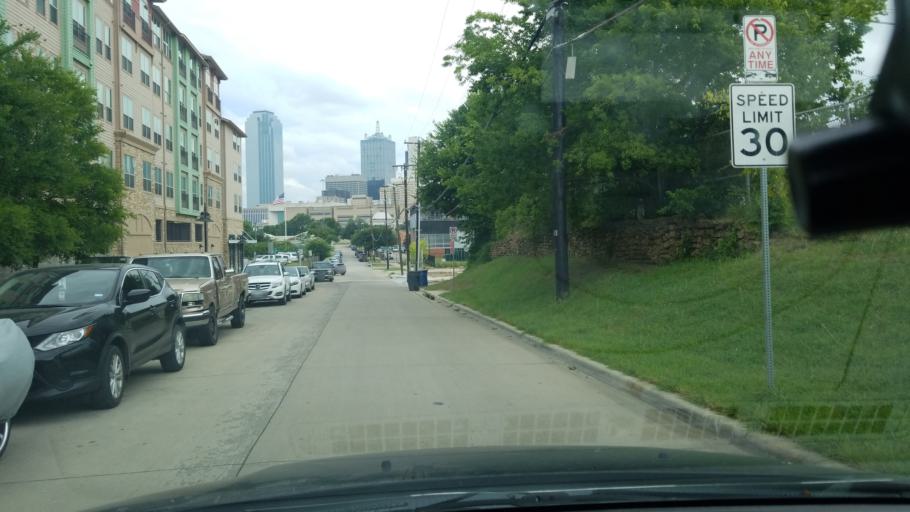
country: US
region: Texas
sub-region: Dallas County
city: Dallas
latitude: 32.7708
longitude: -96.7911
